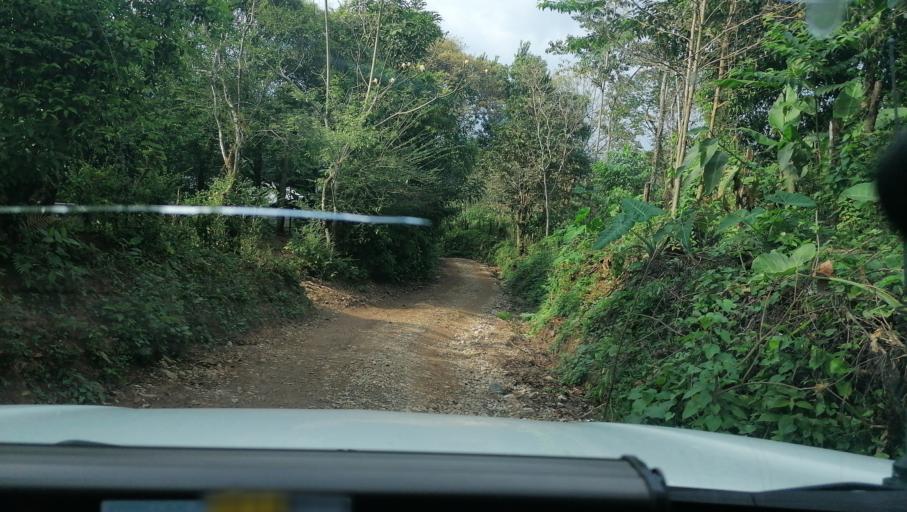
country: MX
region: Chiapas
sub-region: Tapilula
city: San Francisco Jacona
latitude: 17.3279
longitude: -93.1007
